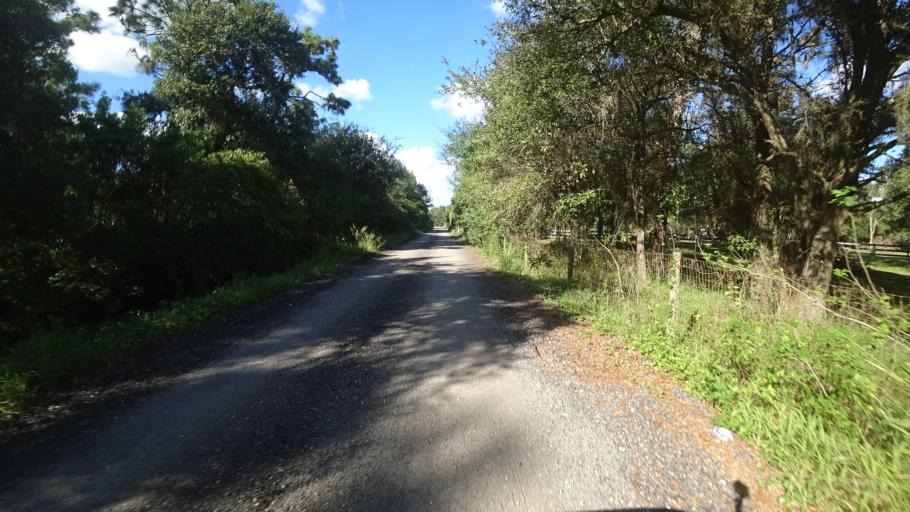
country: US
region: Florida
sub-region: Sarasota County
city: The Meadows
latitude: 27.4659
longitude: -82.3155
